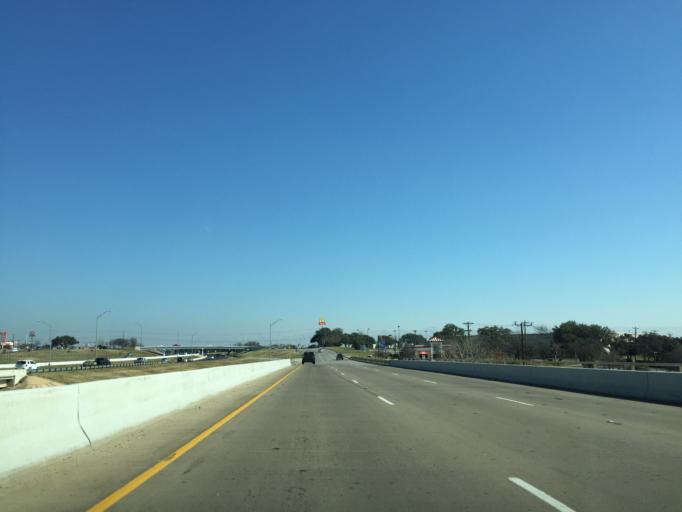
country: US
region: Texas
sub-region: Williamson County
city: Georgetown
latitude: 30.6459
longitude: -97.6828
